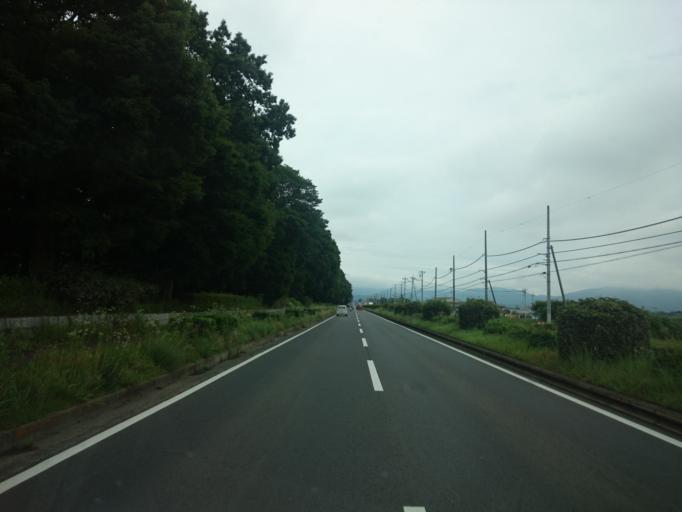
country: JP
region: Ibaraki
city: Tsukuba
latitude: 36.1248
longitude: 140.0748
